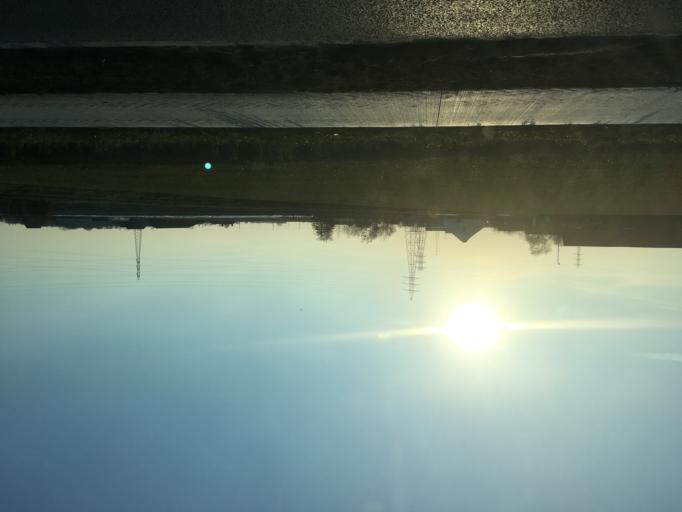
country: BE
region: Flanders
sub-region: Provincie West-Vlaanderen
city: Pittem
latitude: 50.9816
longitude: 3.2688
